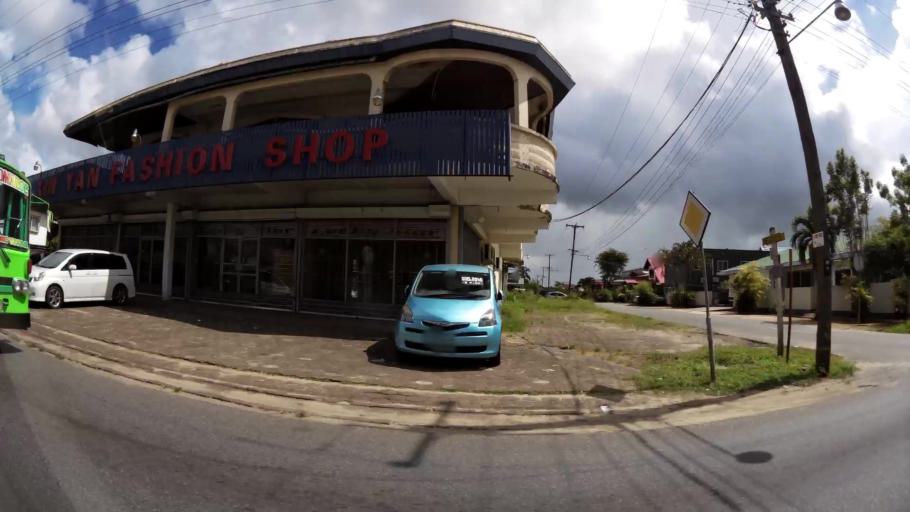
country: SR
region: Paramaribo
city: Paramaribo
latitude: 5.8321
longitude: -55.1913
